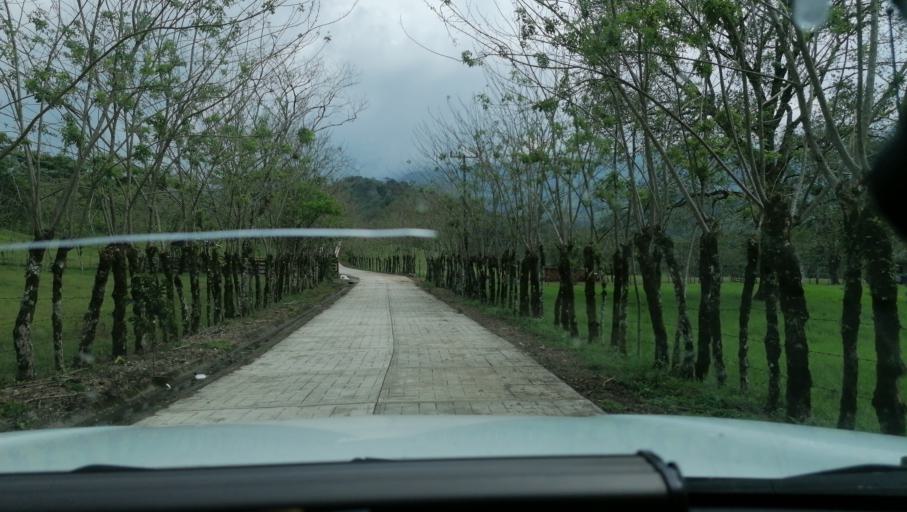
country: MX
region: Chiapas
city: Ocotepec
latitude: 17.3269
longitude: -93.1712
